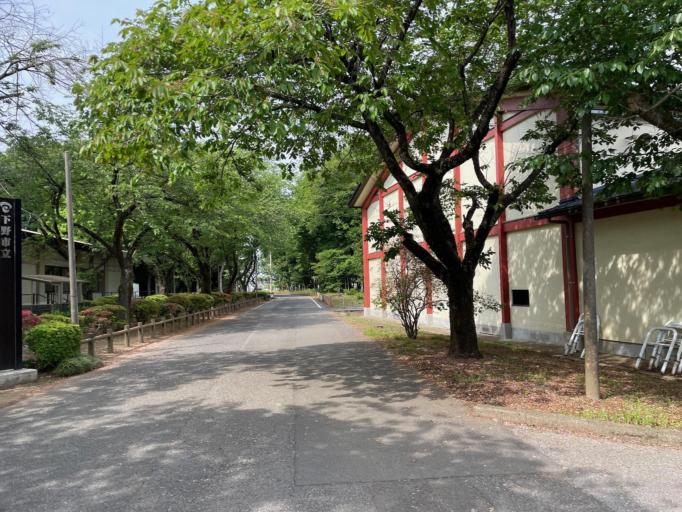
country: JP
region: Tochigi
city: Mibu
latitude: 36.3853
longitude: 139.8110
